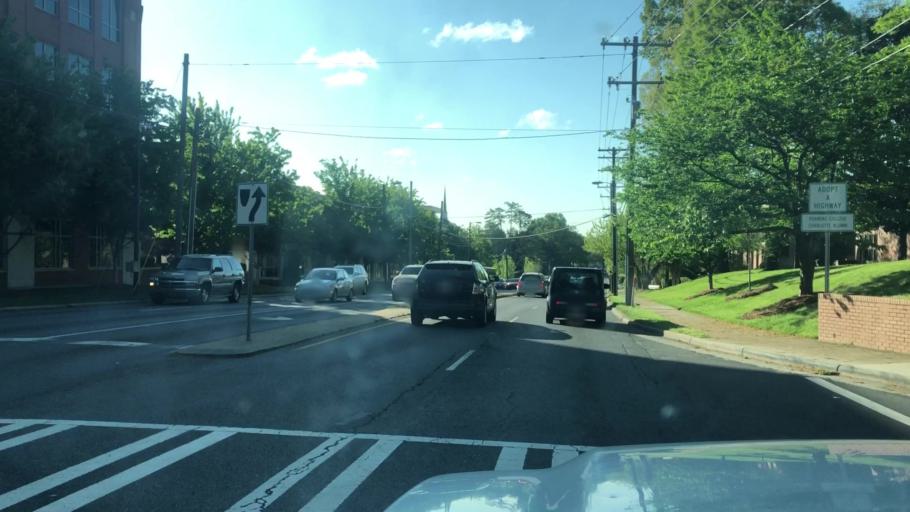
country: US
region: North Carolina
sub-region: Mecklenburg County
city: Charlotte
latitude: 35.1712
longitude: -80.8082
